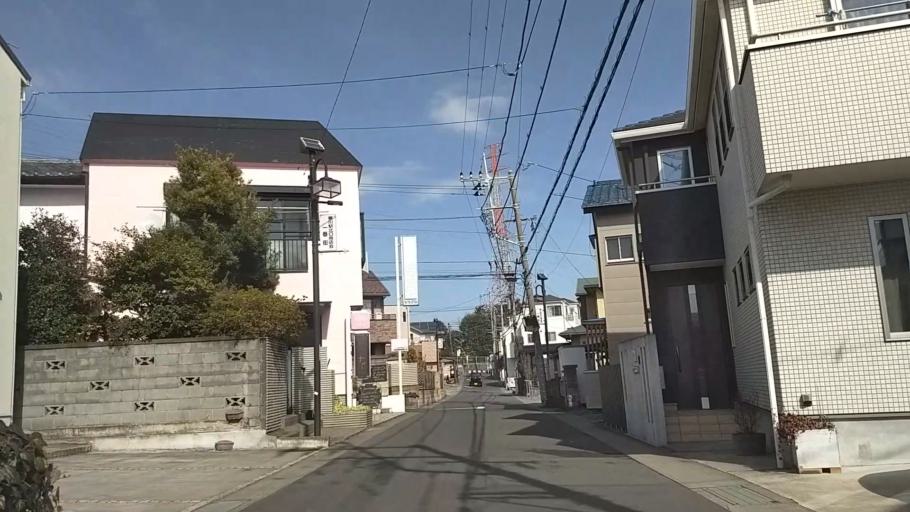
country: JP
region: Kanagawa
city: Chigasaki
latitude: 35.3715
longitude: 139.3891
